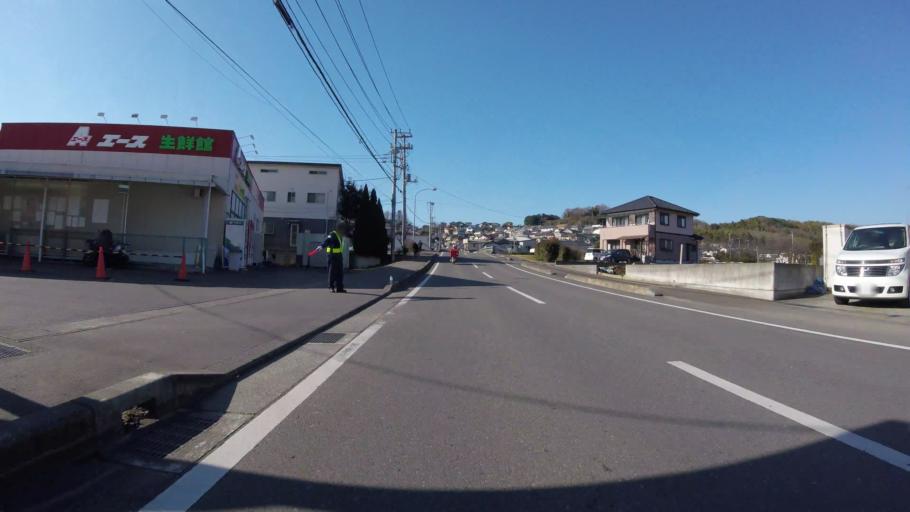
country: JP
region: Shizuoka
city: Mishima
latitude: 35.0872
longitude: 138.9673
